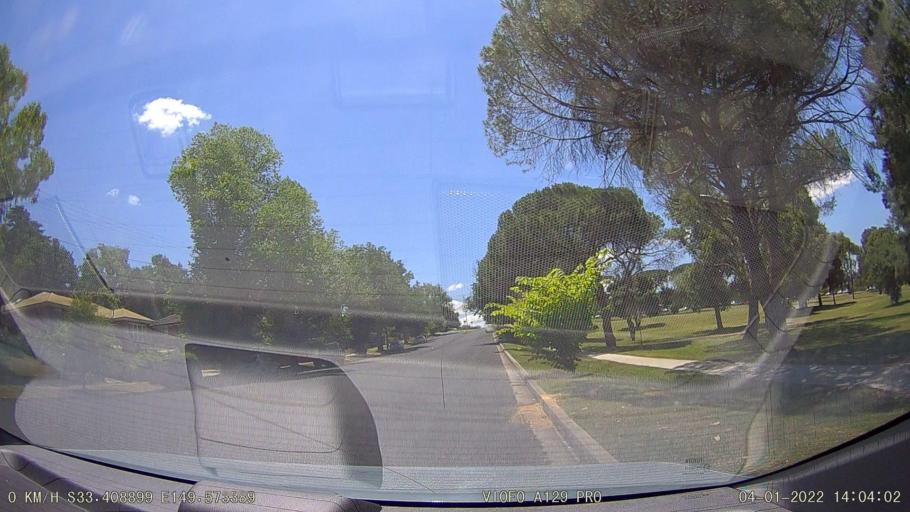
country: AU
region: New South Wales
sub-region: Bathurst Regional
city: Bathurst
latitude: -33.4089
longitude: 149.5734
